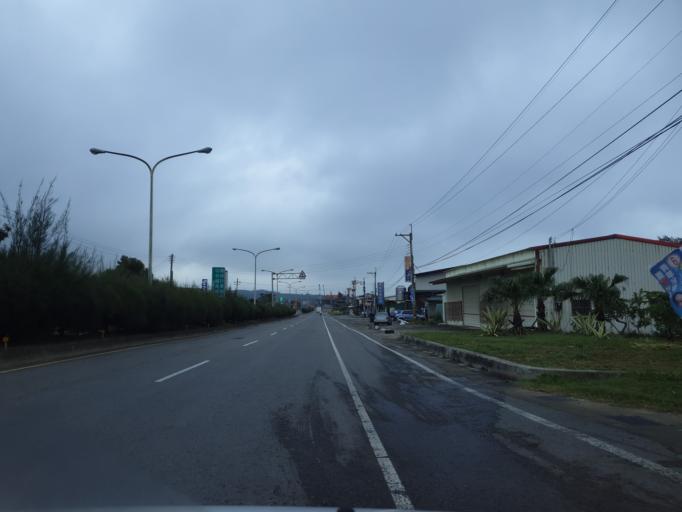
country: TW
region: Taiwan
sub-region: Hsinchu
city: Zhubei
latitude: 24.9077
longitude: 120.9767
